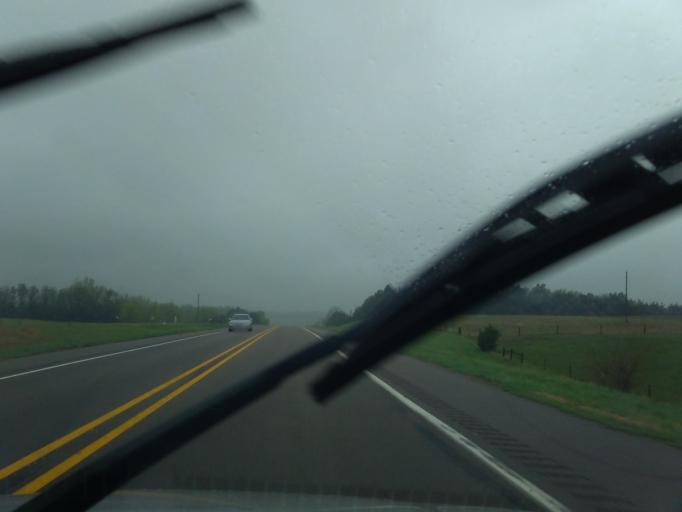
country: US
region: Nebraska
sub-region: Madison County
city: Norfolk
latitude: 42.0960
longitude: -97.3185
